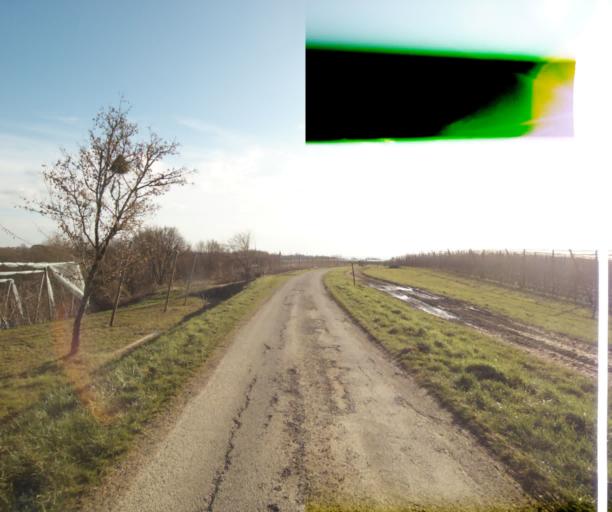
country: FR
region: Midi-Pyrenees
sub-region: Departement du Tarn-et-Garonne
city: Moissac
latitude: 44.1375
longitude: 1.0551
